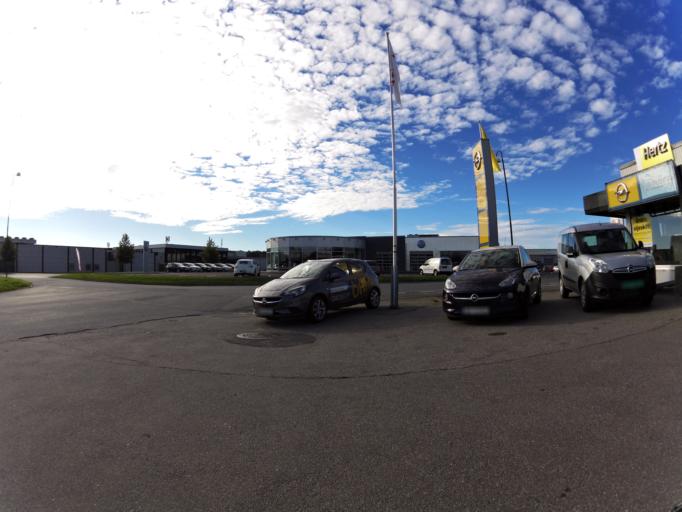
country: NO
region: Ostfold
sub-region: Sarpsborg
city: Sarpsborg
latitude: 59.2884
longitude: 11.0895
